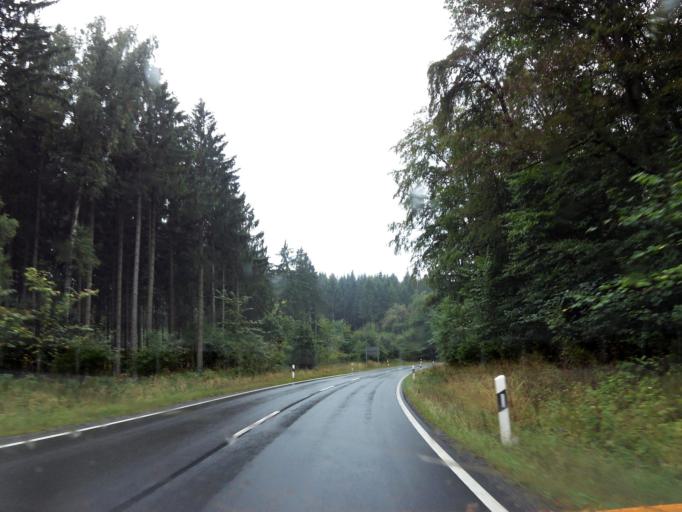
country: DE
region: Saxony-Anhalt
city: Harzgerode
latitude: 51.6796
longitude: 11.1433
